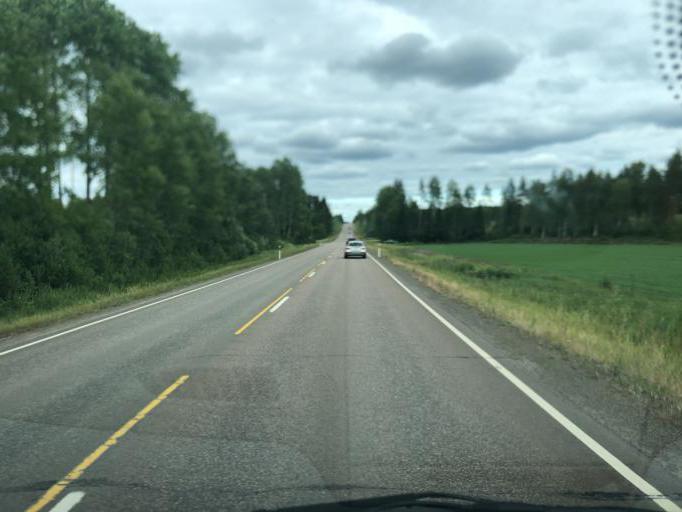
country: FI
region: Kymenlaakso
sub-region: Kouvola
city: Kouvola
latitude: 61.0462
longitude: 27.0199
